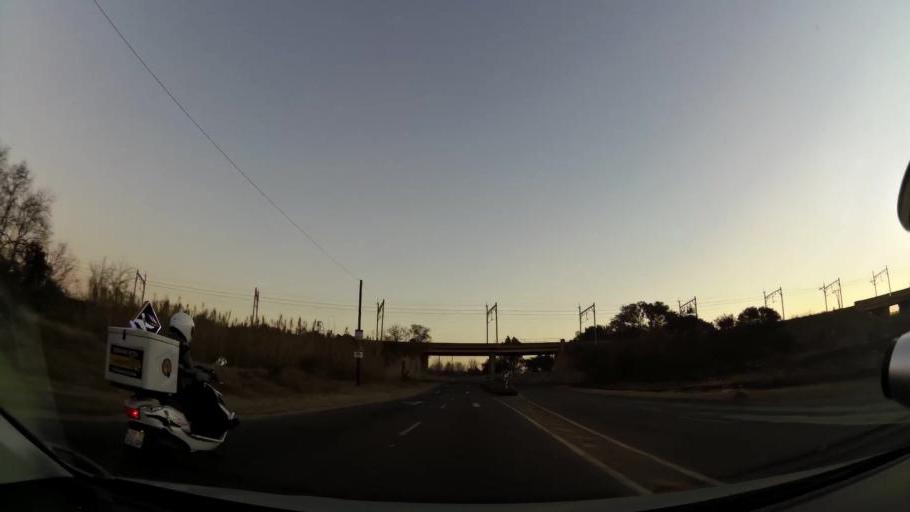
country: ZA
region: Gauteng
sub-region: City of Tshwane Metropolitan Municipality
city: Pretoria
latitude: -25.7374
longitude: 28.1647
